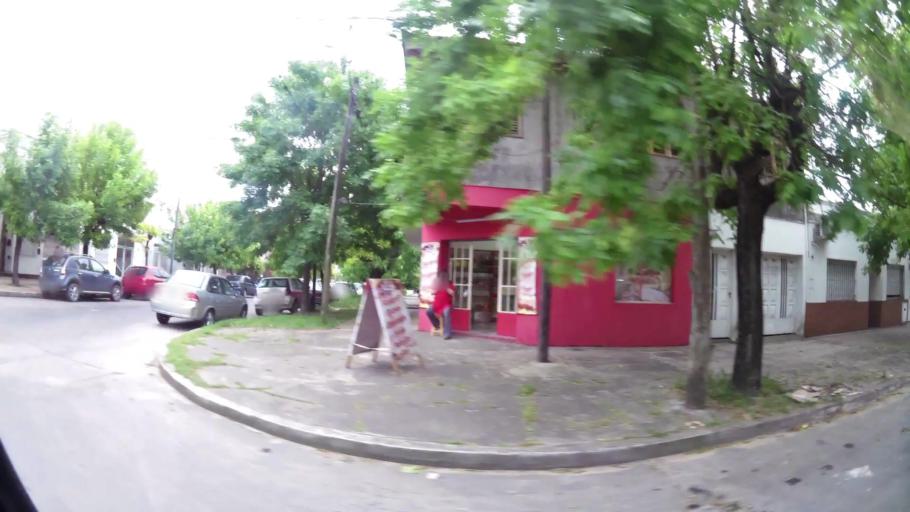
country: AR
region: Buenos Aires
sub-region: Partido de La Plata
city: La Plata
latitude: -34.9262
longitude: -57.9868
